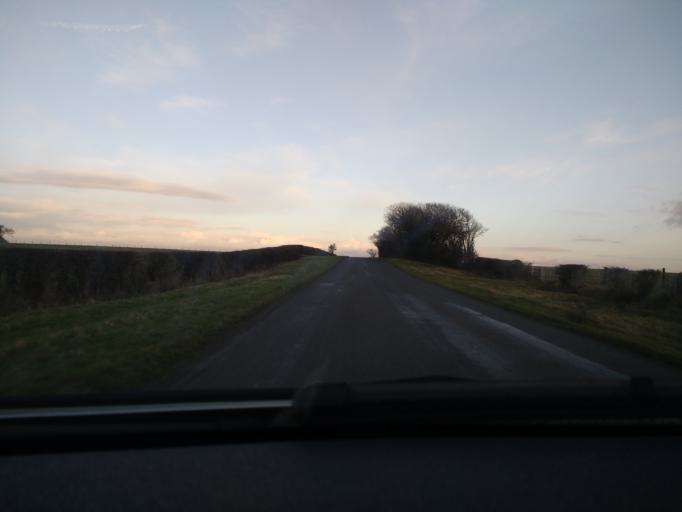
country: GB
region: England
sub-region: Cumbria
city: Carlisle
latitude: 54.7312
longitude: -2.9589
